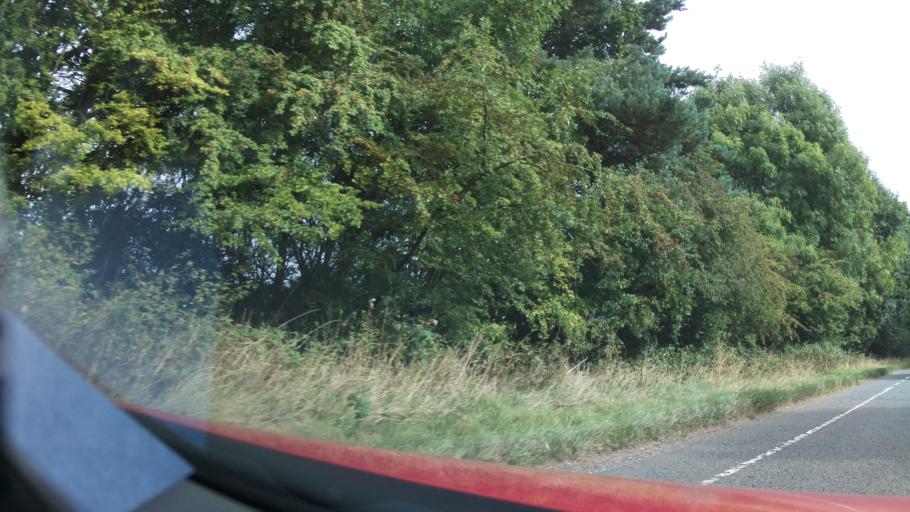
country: GB
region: England
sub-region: Telford and Wrekin
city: Newport
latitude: 52.7789
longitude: -2.3667
